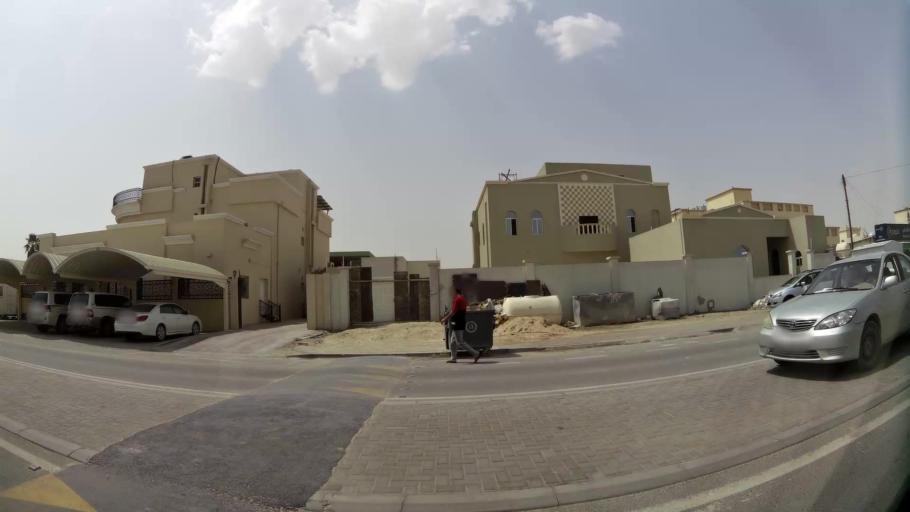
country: QA
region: Baladiyat ar Rayyan
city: Ar Rayyan
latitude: 25.2315
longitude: 51.4274
